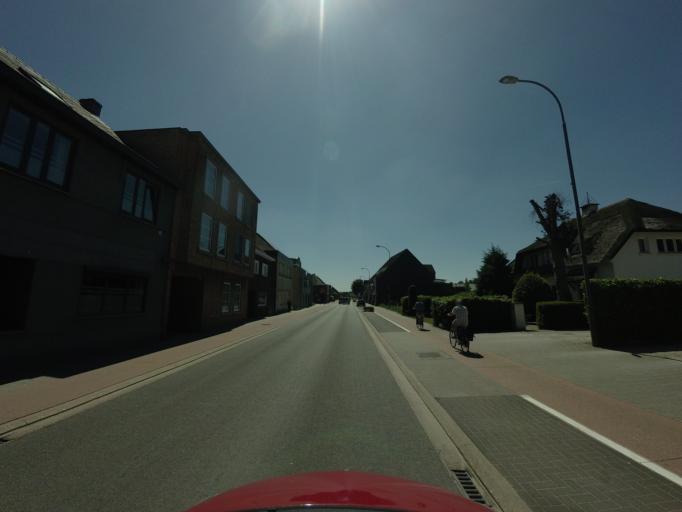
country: BE
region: Flanders
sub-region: Provincie Limburg
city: Lommel
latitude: 51.2280
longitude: 5.3069
